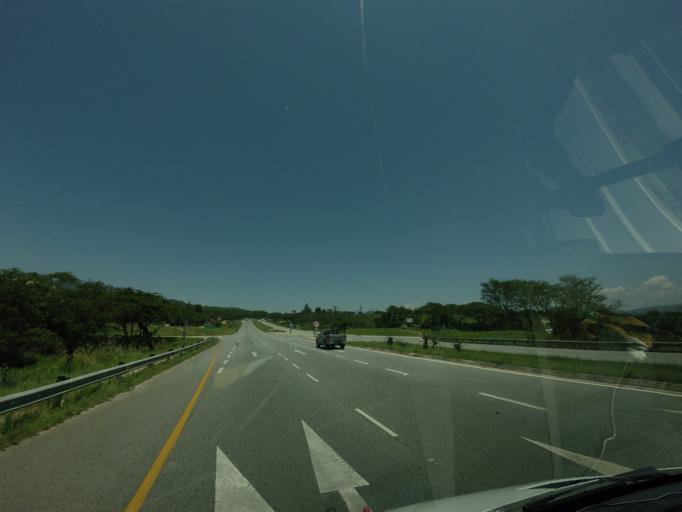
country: ZA
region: Mpumalanga
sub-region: Ehlanzeni District
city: Nelspruit
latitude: -25.4497
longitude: 30.8274
